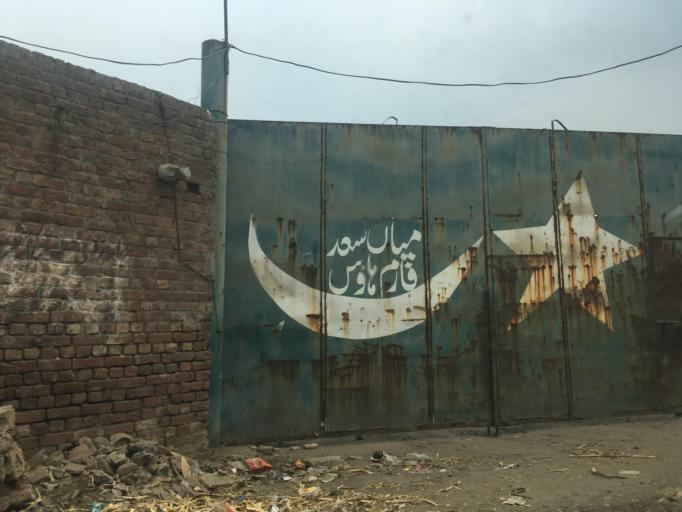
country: PK
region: Punjab
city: Lahore
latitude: 31.6140
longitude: 74.3675
